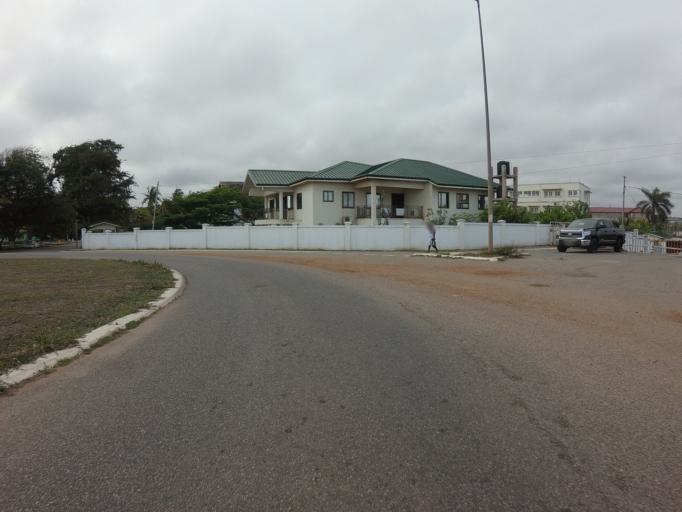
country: GH
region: Greater Accra
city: Accra
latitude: 5.5480
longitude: -0.1864
